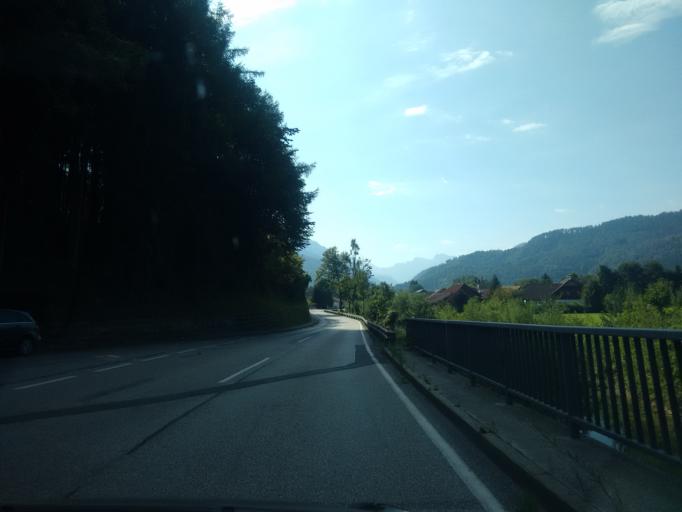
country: AT
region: Upper Austria
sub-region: Politischer Bezirk Gmunden
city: Gruenau im Almtal
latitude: 47.8726
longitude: 13.9436
